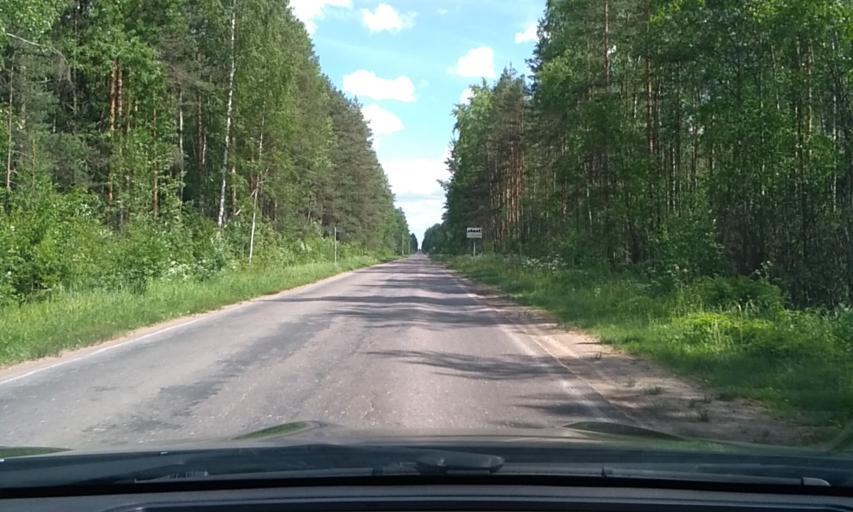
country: RU
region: Leningrad
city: Imeni Sverdlova
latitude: 59.8233
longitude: 30.7356
